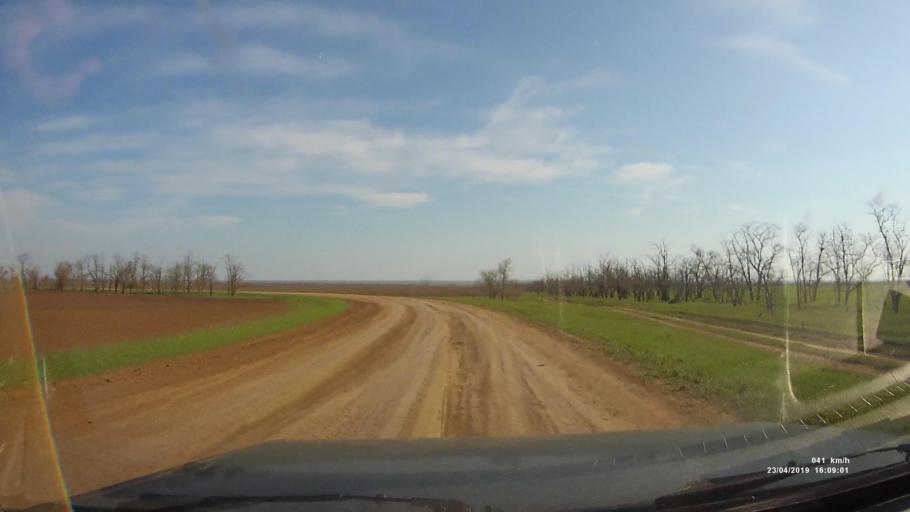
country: RU
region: Rostov
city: Remontnoye
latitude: 46.4824
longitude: 43.1076
